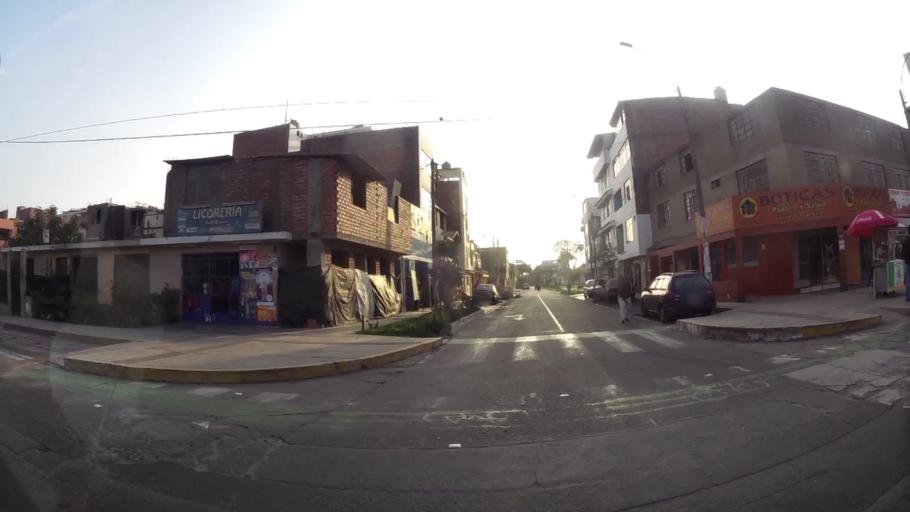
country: PE
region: Lima
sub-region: Lima
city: Independencia
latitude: -11.9801
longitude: -77.0725
